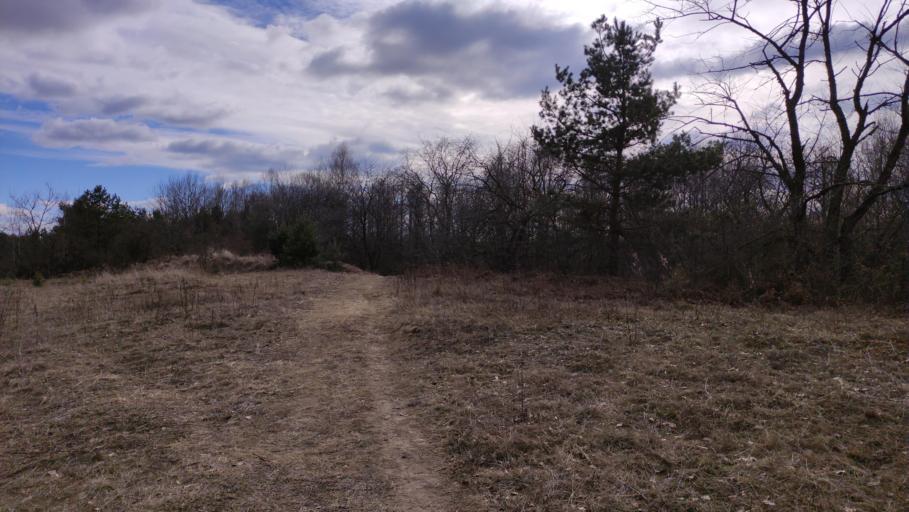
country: LT
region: Alytaus apskritis
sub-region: Alytus
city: Alytus
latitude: 54.4099
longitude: 24.0516
